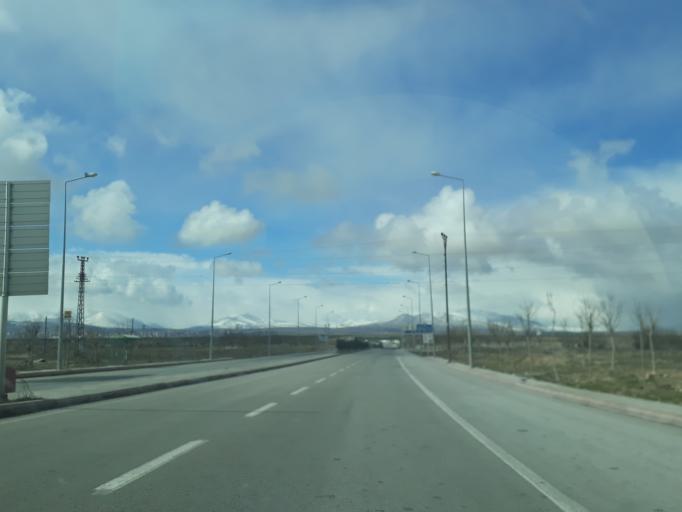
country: TR
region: Konya
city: Asagipinarbasi
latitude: 37.9925
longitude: 32.5916
